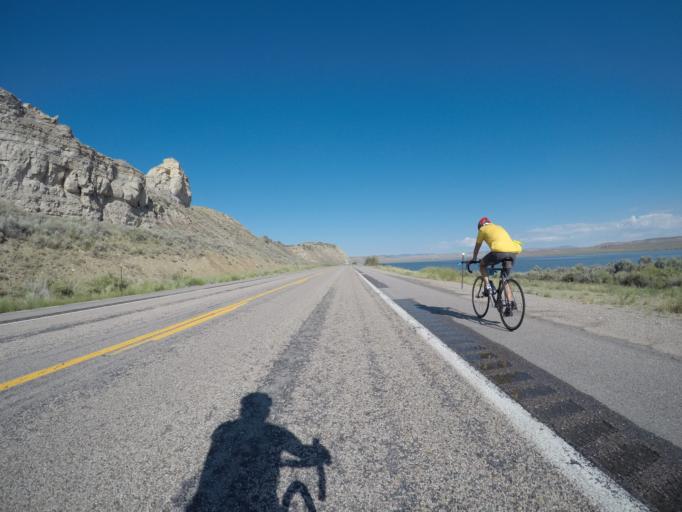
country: US
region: Wyoming
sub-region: Sublette County
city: Marbleton
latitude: 42.1117
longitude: -110.1448
